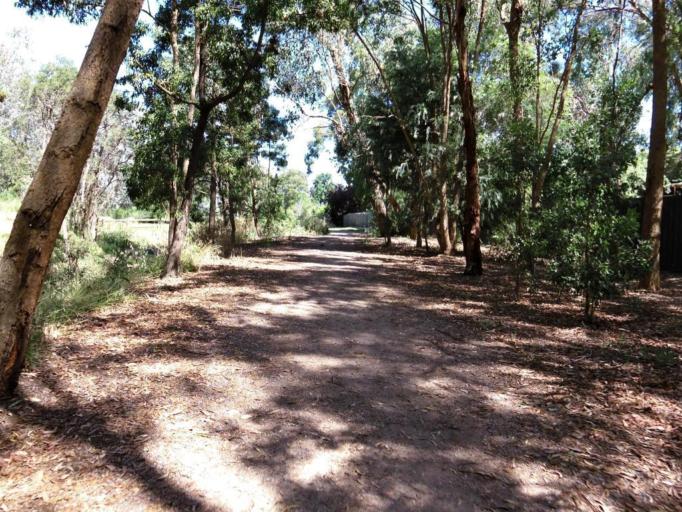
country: AU
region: Victoria
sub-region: Maroondah
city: Croydon North
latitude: -37.7766
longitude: 145.3024
